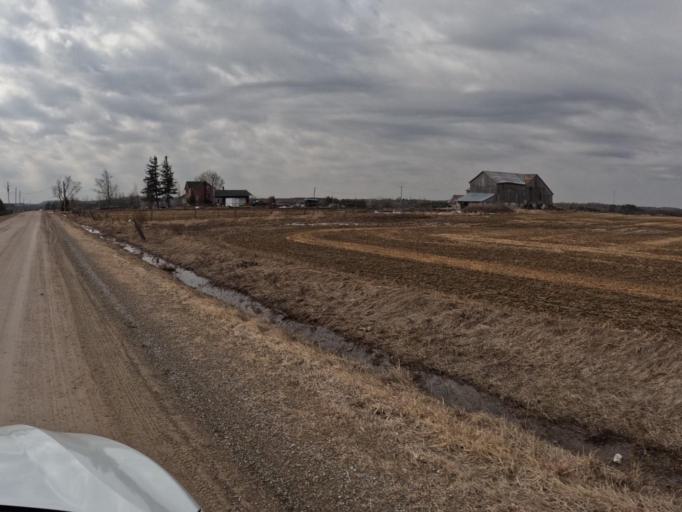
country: CA
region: Ontario
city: Orangeville
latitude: 43.9094
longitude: -80.2153
